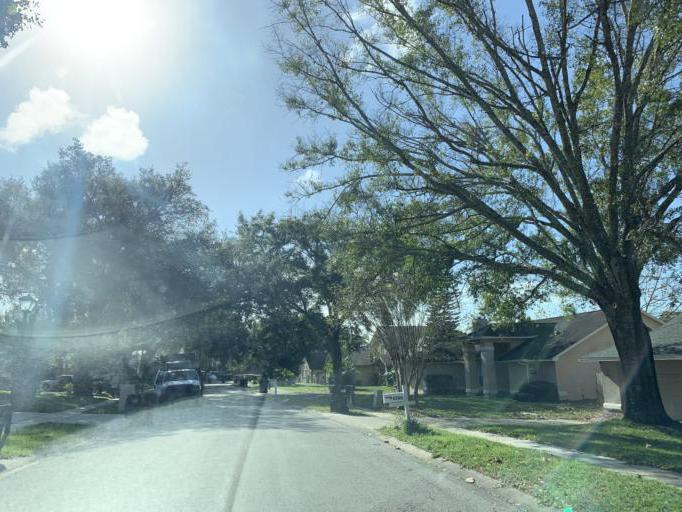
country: US
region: Florida
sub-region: Orange County
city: Clarcona
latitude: 28.6311
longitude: -81.4727
